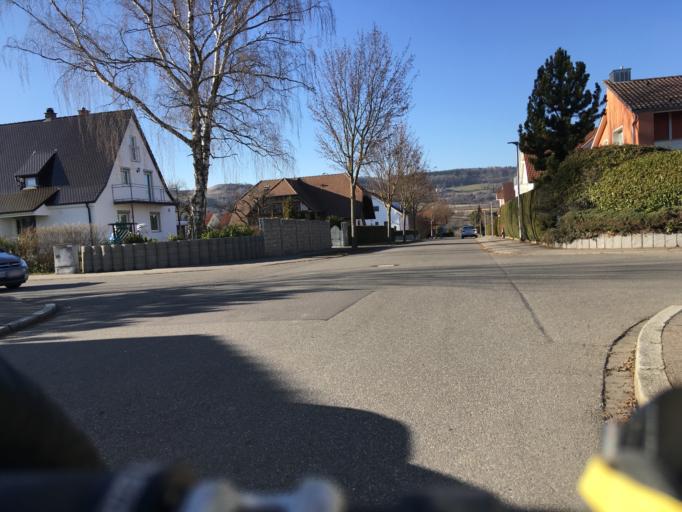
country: DE
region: Baden-Wuerttemberg
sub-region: Freiburg Region
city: Singen
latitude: 47.7715
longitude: 8.8302
